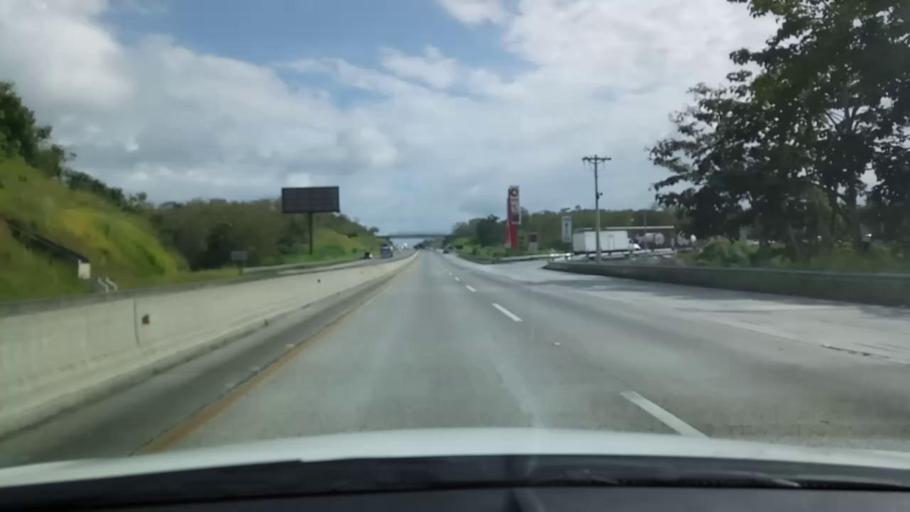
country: PA
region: Colon
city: El Giral
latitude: 9.2495
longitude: -79.6888
